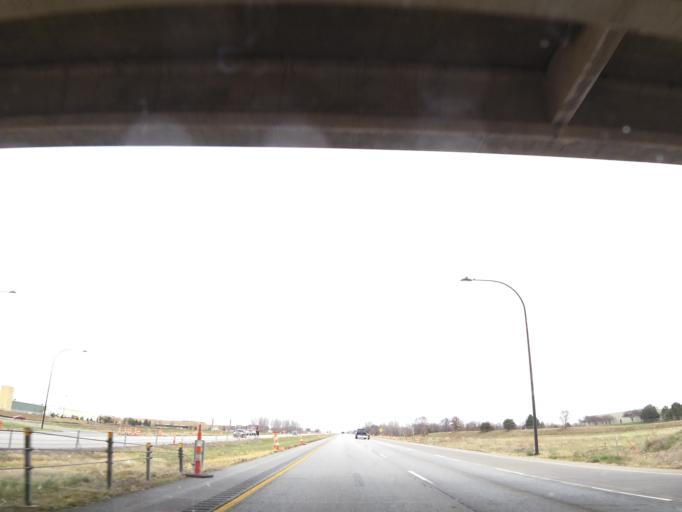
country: US
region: Iowa
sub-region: Scott County
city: Bettendorf
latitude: 41.5747
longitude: -90.5221
